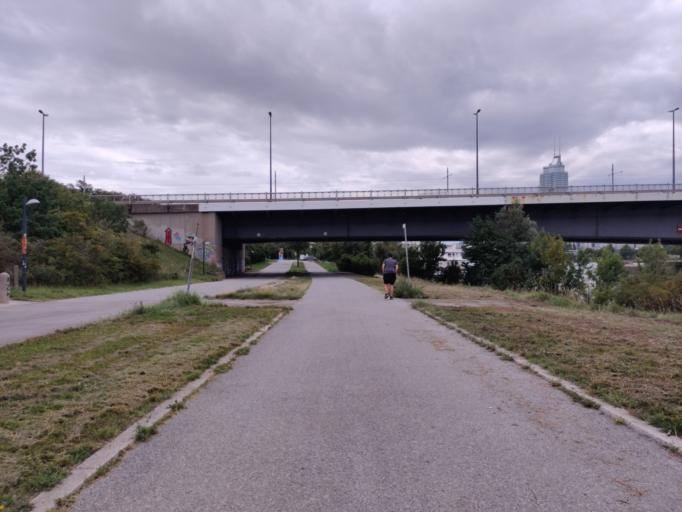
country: AT
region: Vienna
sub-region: Wien Stadt
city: Vienna
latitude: 48.2485
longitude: 16.3857
